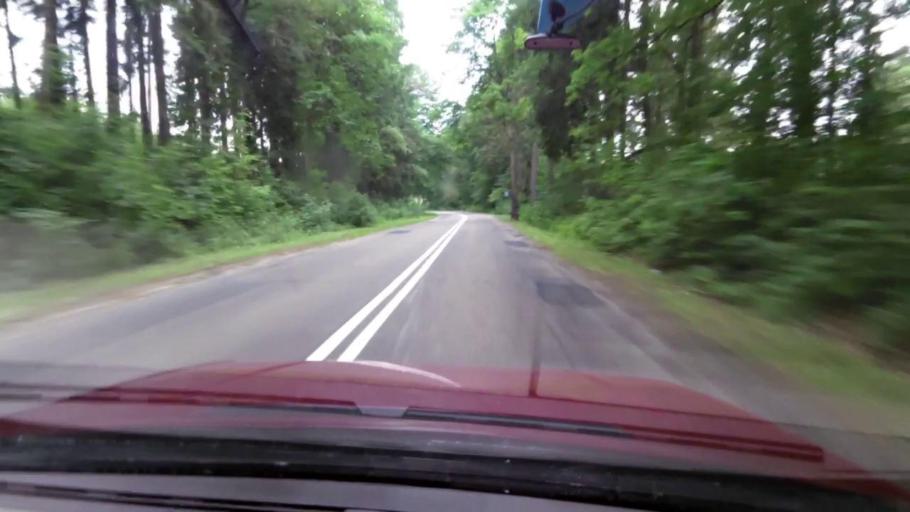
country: PL
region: West Pomeranian Voivodeship
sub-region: Powiat koszalinski
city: Sianow
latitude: 54.1871
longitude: 16.2665
